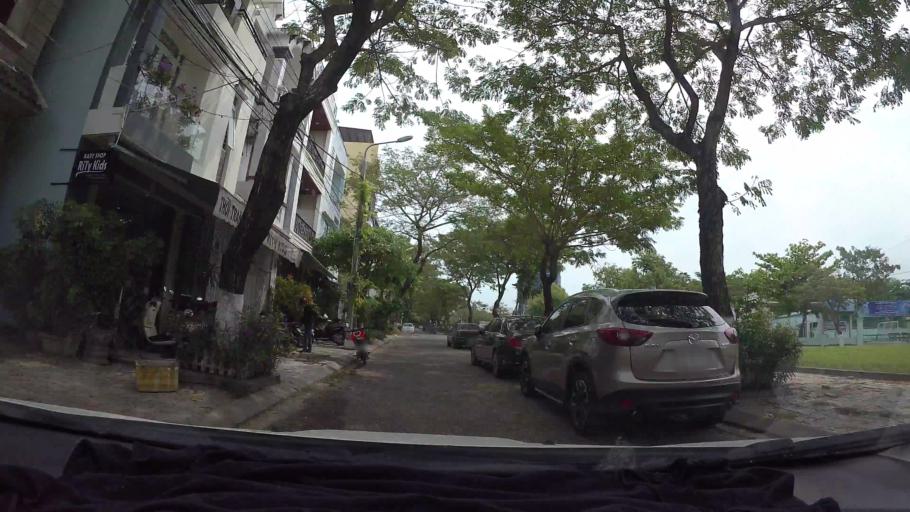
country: VN
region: Da Nang
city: Da Nang
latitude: 16.0877
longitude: 108.2172
